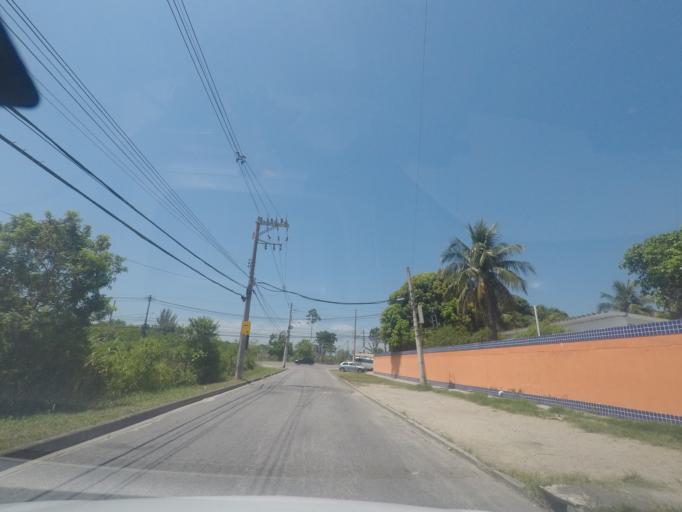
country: BR
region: Rio de Janeiro
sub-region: Nilopolis
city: Nilopolis
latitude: -22.9850
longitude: -43.4595
